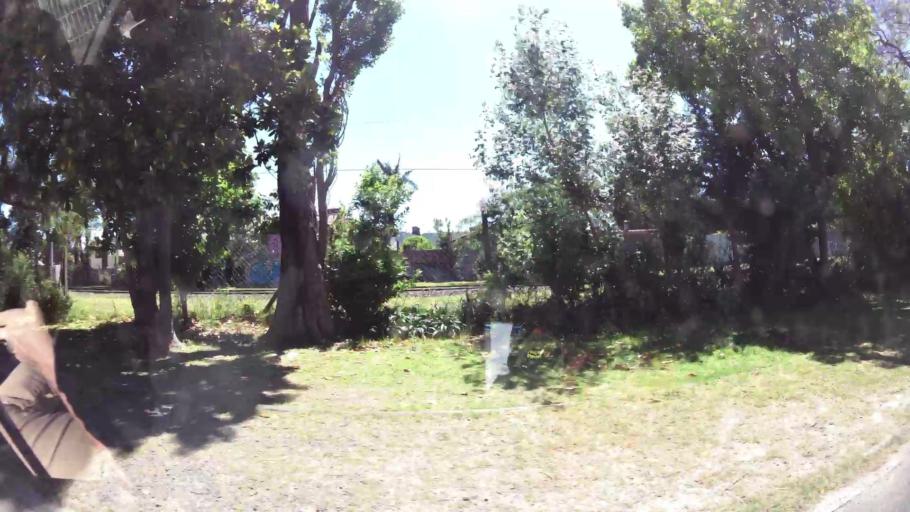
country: AR
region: Buenos Aires
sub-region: Partido de General San Martin
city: General San Martin
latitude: -34.5276
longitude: -58.5417
